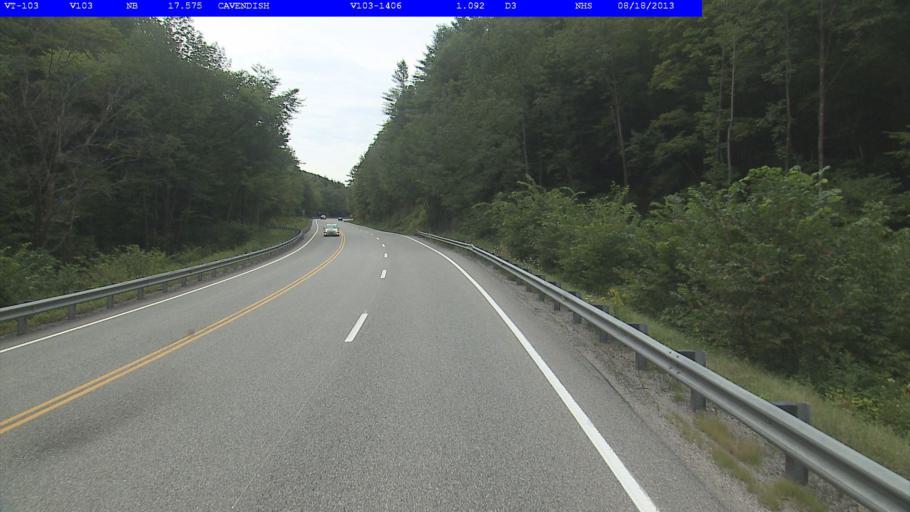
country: US
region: Vermont
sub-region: Windsor County
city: Chester
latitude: 43.3629
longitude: -72.6341
